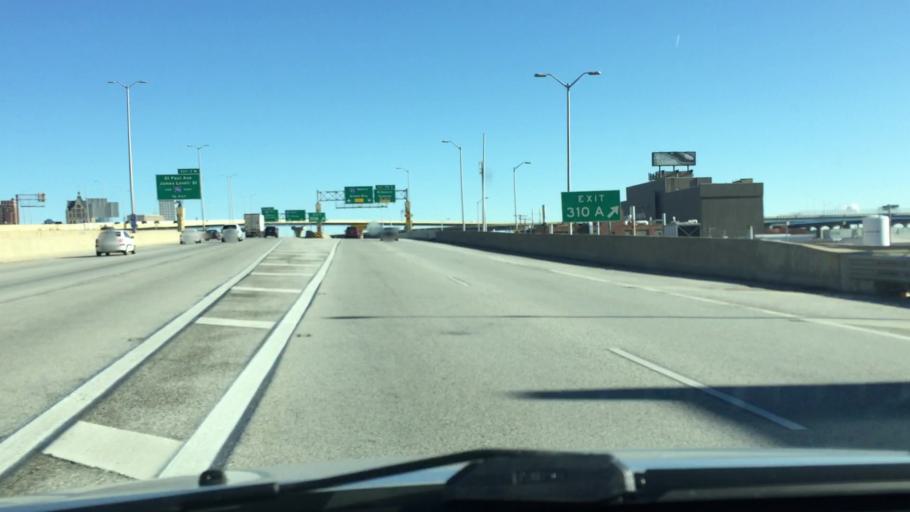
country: US
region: Wisconsin
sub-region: Milwaukee County
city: Milwaukee
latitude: 43.0353
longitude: -87.9309
